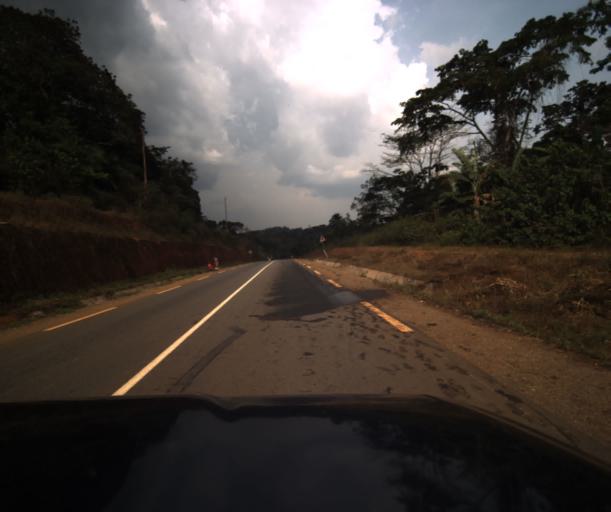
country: CM
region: Centre
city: Mbankomo
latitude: 3.6532
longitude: 11.3365
